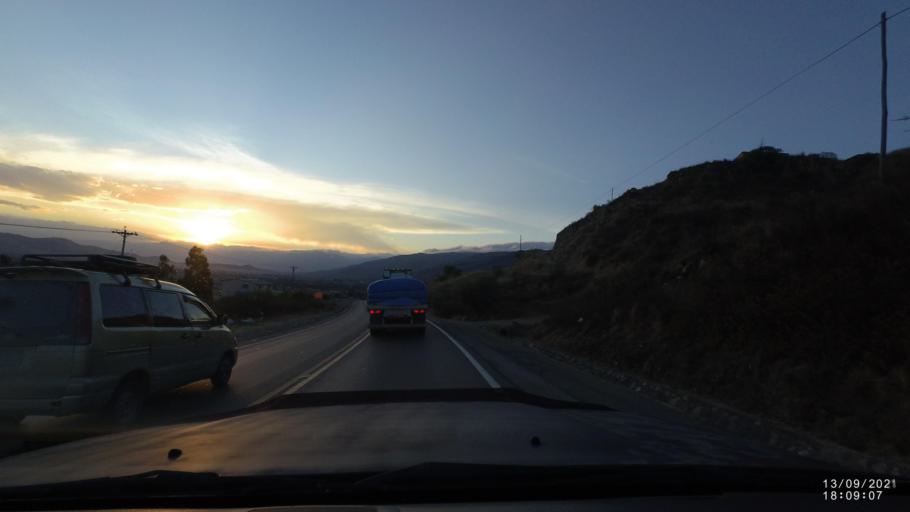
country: BO
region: Cochabamba
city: Colomi
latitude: -17.4115
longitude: -65.9652
